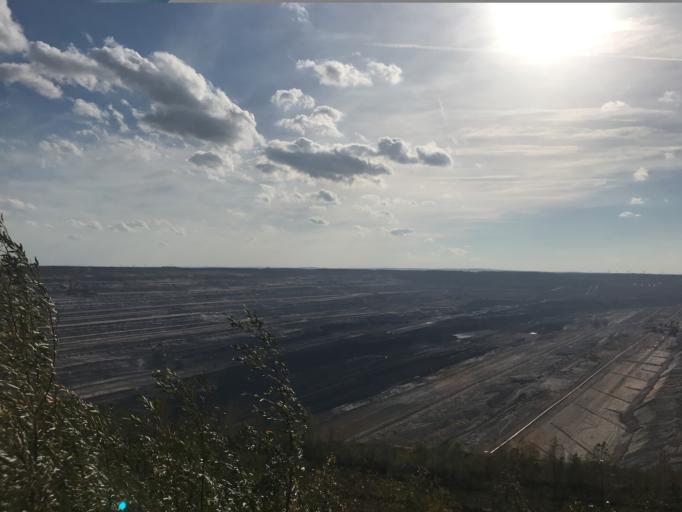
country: DE
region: North Rhine-Westphalia
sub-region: Regierungsbezirk Koln
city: Elsdorf
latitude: 50.9270
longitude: 6.5588
